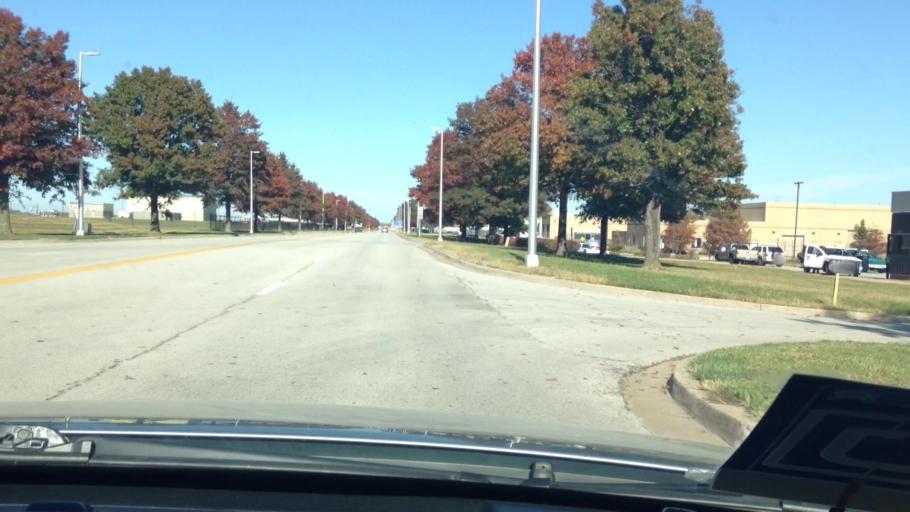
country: US
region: Missouri
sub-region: Platte County
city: Weatherby Lake
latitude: 39.3084
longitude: -94.7174
